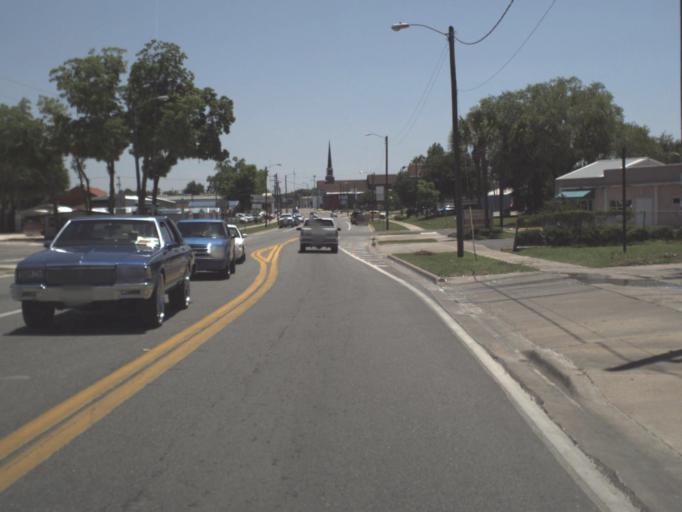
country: US
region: Florida
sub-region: Suwannee County
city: Live Oak
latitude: 30.2995
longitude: -82.9916
